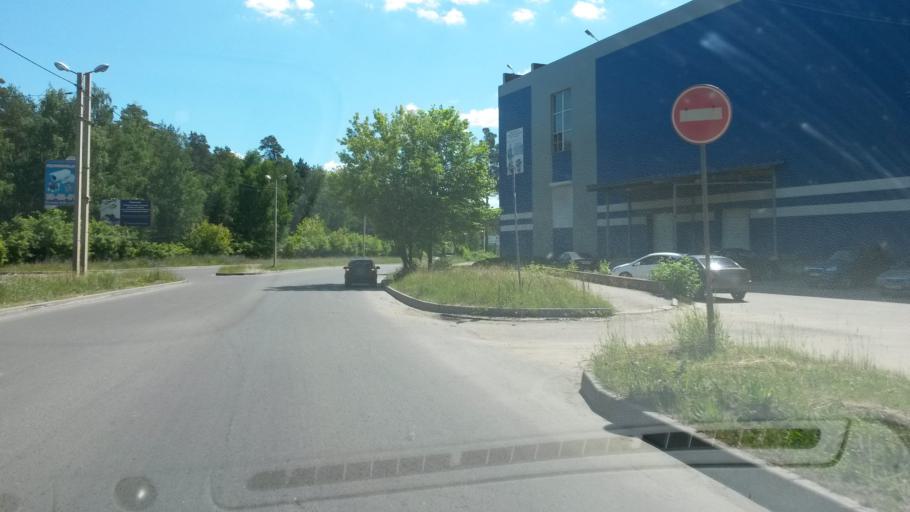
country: RU
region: Ivanovo
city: Kokhma
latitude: 56.9691
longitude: 41.0571
